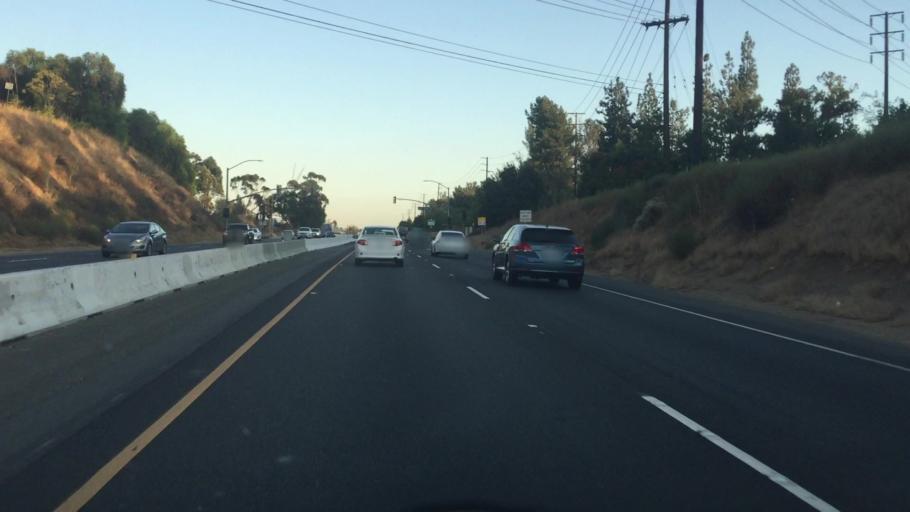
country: US
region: California
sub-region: Los Angeles County
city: Pomona
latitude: 34.0445
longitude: -117.7718
